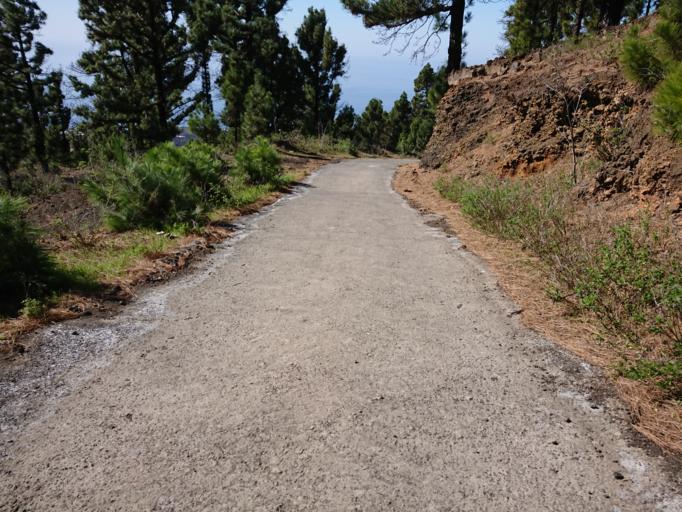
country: ES
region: Canary Islands
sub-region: Provincia de Santa Cruz de Tenerife
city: El Paso
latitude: 28.6071
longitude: -17.8641
